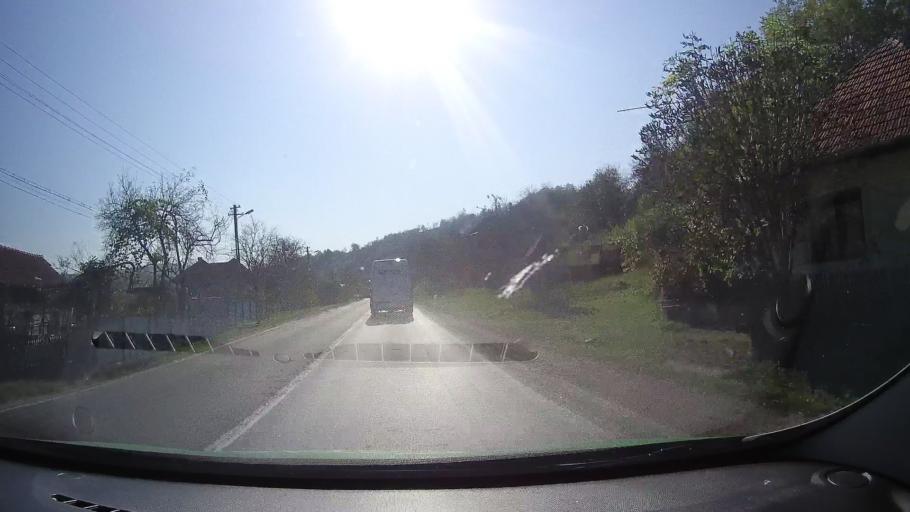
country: RO
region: Hunedoara
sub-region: Comuna Dobra
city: Dobra
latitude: 45.9108
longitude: 22.5744
